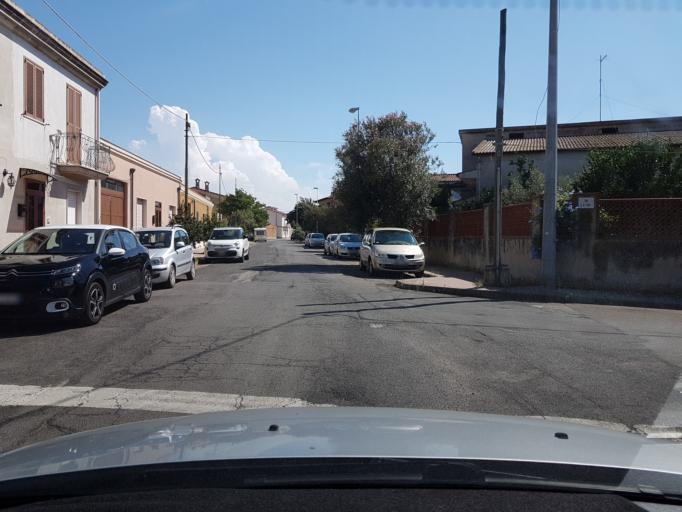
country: IT
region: Sardinia
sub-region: Provincia di Oristano
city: Cabras
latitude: 39.9343
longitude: 8.5313
